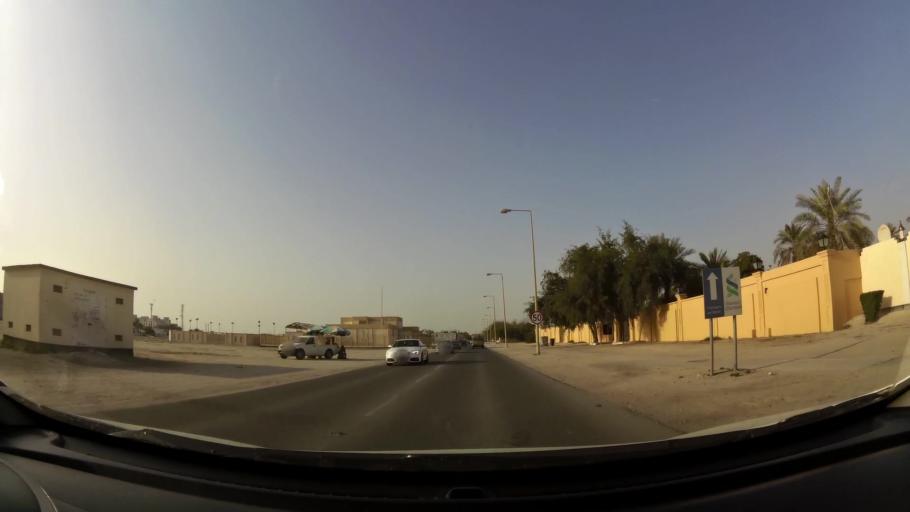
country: BH
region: Manama
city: Jidd Hafs
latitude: 26.2134
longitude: 50.4803
